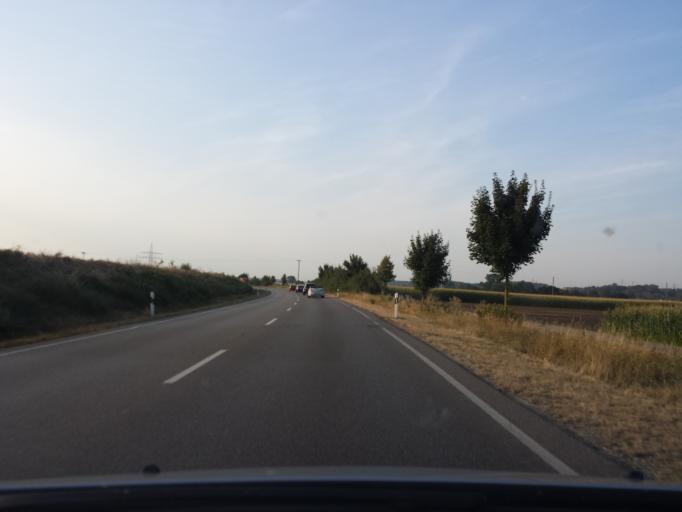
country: DE
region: Bavaria
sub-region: Swabia
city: Friedberg
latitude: 48.3782
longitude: 10.9618
